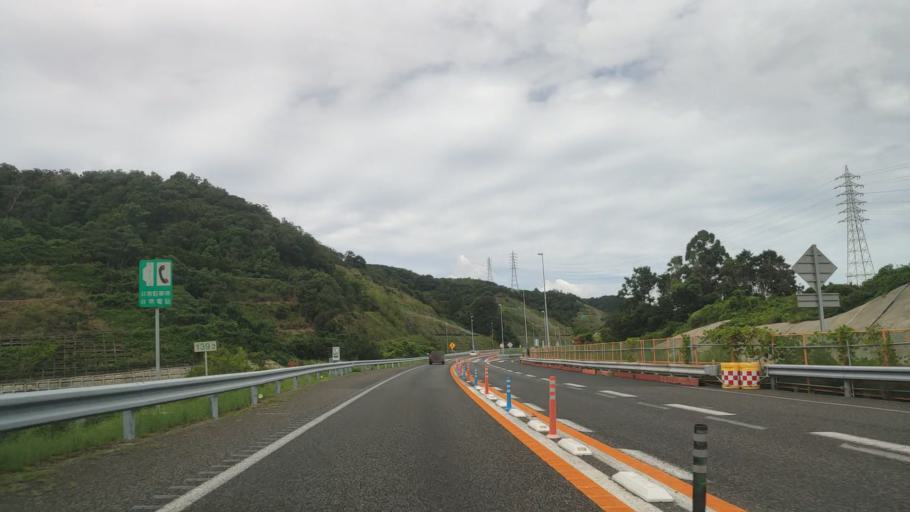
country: JP
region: Wakayama
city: Gobo
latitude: 33.8252
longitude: 135.2201
